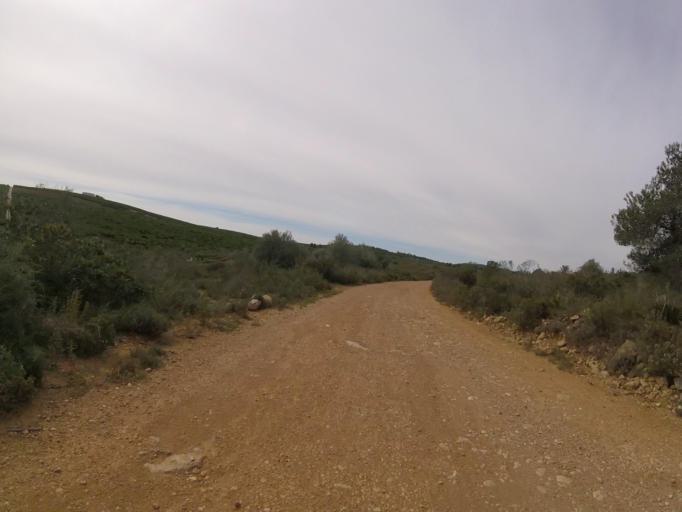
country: ES
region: Valencia
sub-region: Provincia de Castello
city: Torreblanca
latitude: 40.1986
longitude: 0.1354
